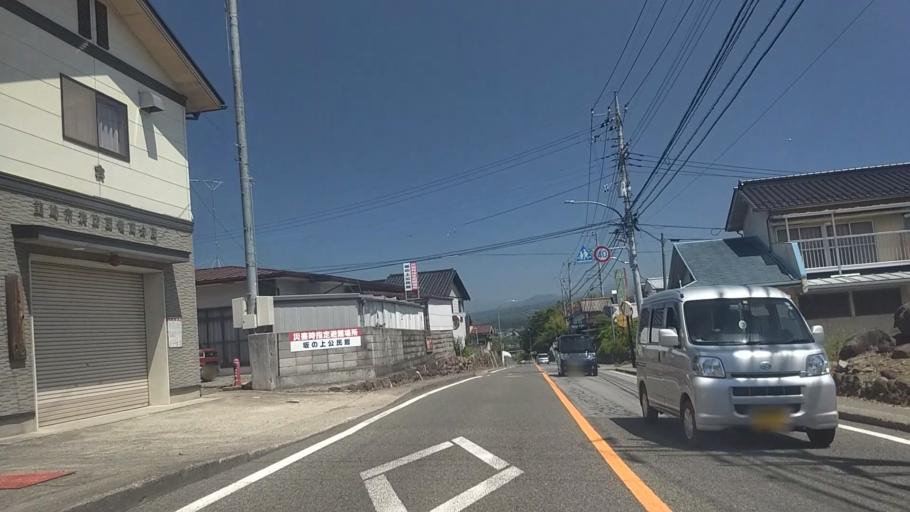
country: JP
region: Yamanashi
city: Nirasaki
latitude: 35.6821
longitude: 138.4630
